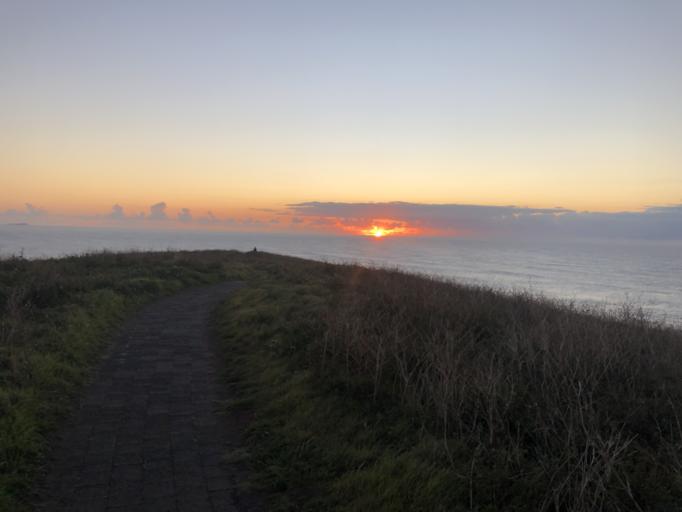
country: AU
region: New South Wales
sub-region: Coffs Harbour
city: Coffs Harbour
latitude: -30.3052
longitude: 153.1521
